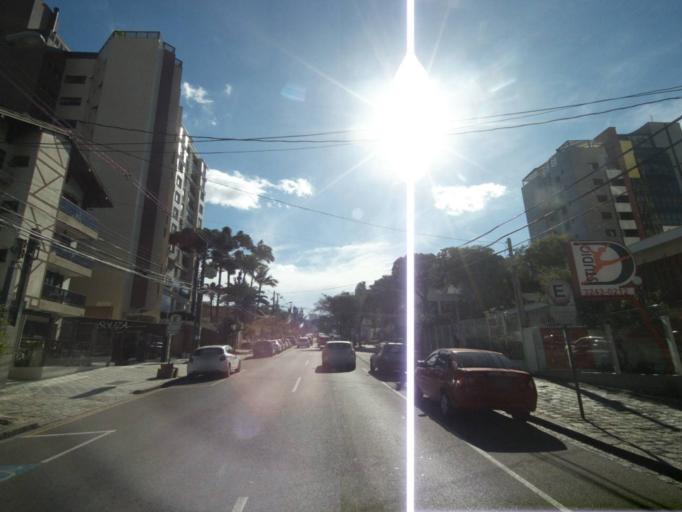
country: BR
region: Parana
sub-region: Curitiba
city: Curitiba
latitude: -25.4399
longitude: -49.2875
